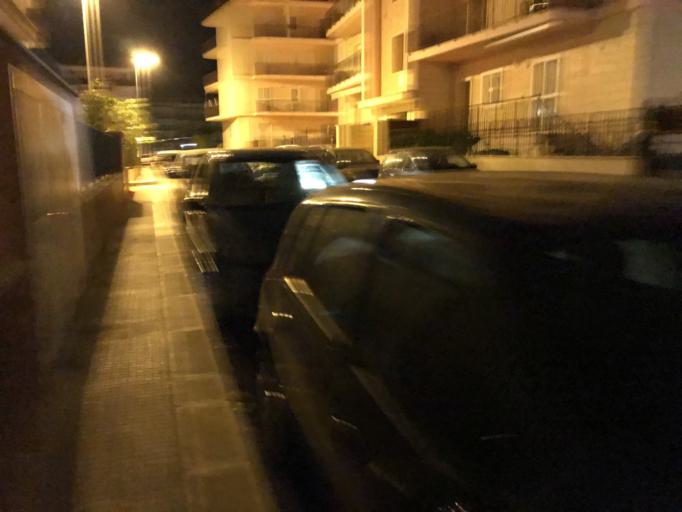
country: IT
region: Apulia
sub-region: Provincia di Bari
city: Corato
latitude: 41.1535
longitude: 16.4023
